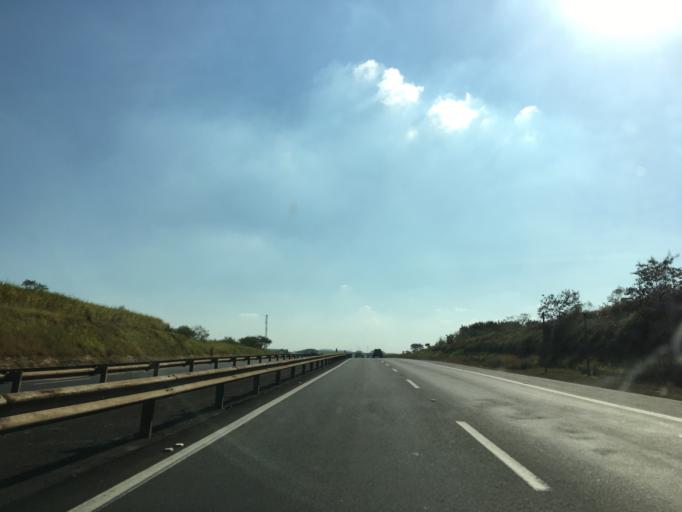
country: BR
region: Sao Paulo
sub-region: Piracicaba
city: Piracicaba
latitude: -22.7277
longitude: -47.5502
